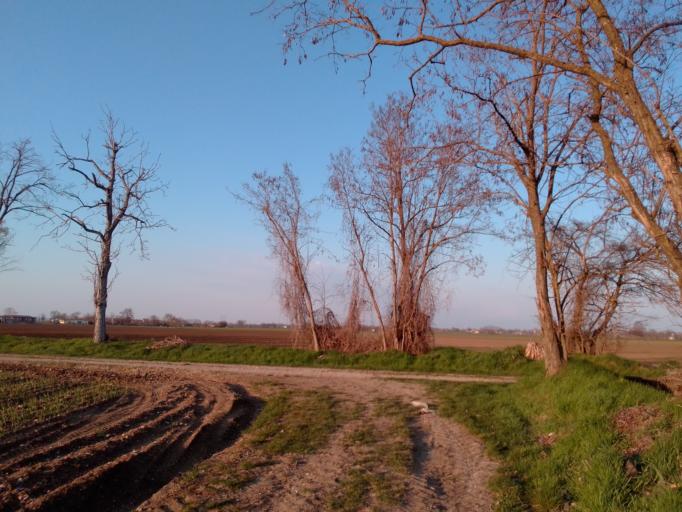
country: IT
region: Emilia-Romagna
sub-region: Provincia di Piacenza
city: Borgonovo Valtidone
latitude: 45.0007
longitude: 9.4846
